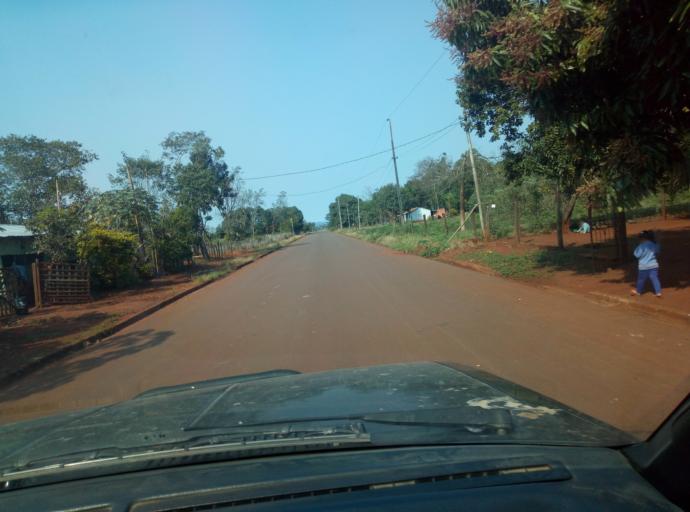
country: PY
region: Caaguazu
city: Carayao
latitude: -25.2139
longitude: -56.2885
